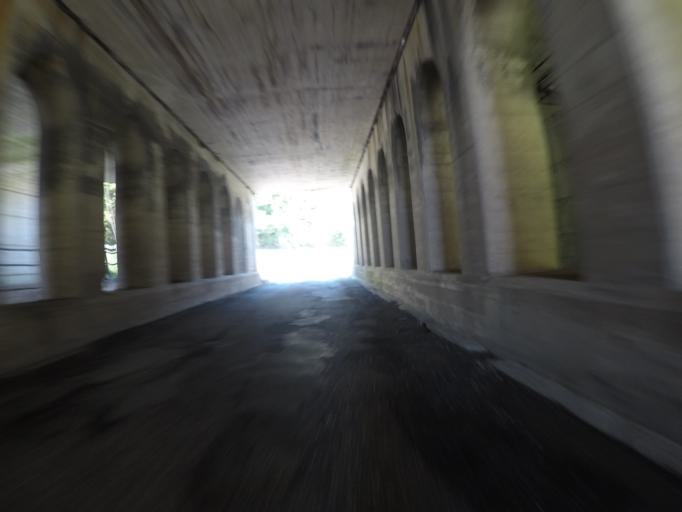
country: US
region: Ohio
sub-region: Lawrence County
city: South Point
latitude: 38.4282
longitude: -82.6025
